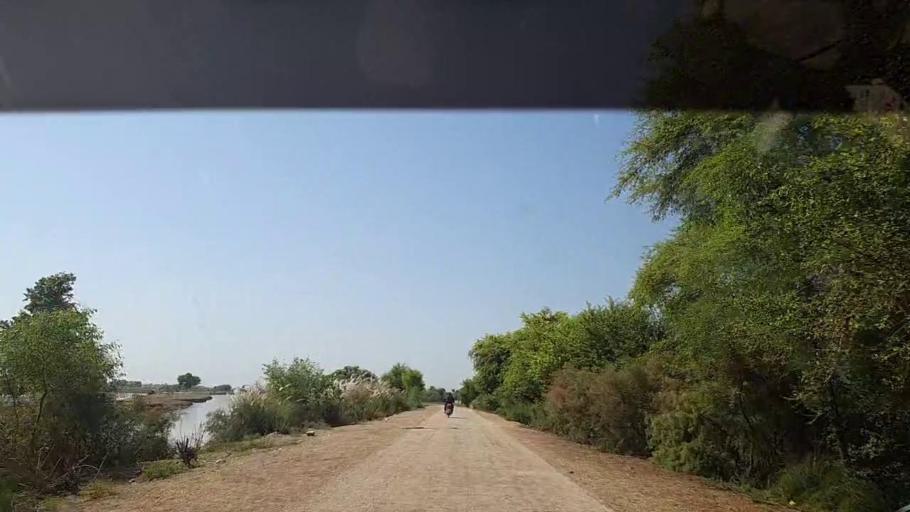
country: PK
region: Sindh
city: Ghauspur
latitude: 28.1915
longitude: 69.0563
